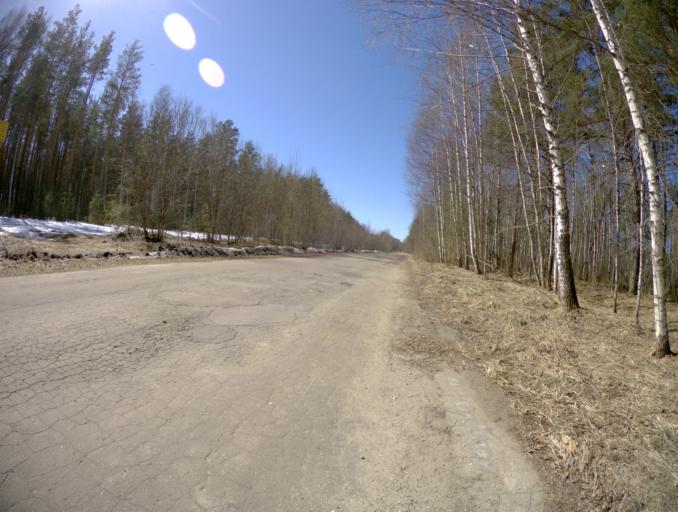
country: RU
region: Vladimir
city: Orgtrud
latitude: 56.2821
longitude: 40.7251
